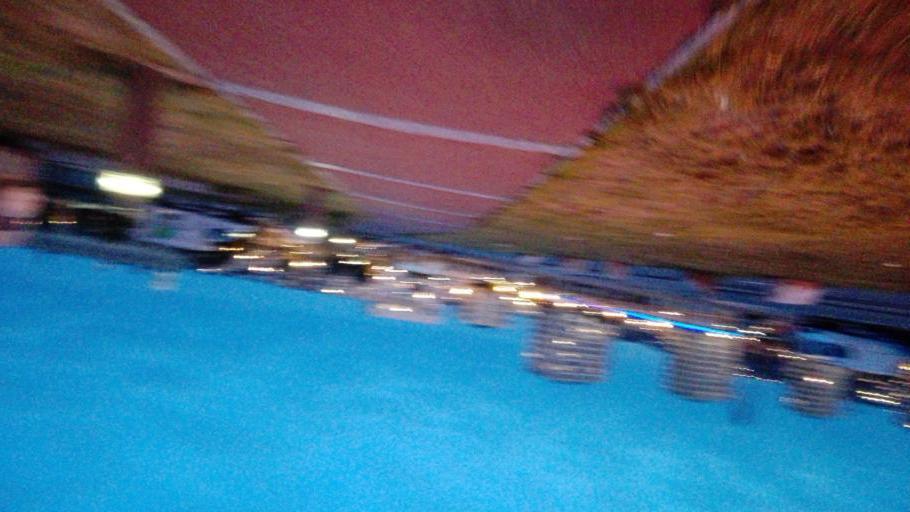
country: FR
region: Nord-Pas-de-Calais
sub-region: Departement du Pas-de-Calais
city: Boulogne-sur-Mer
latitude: 50.7218
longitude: 1.5994
